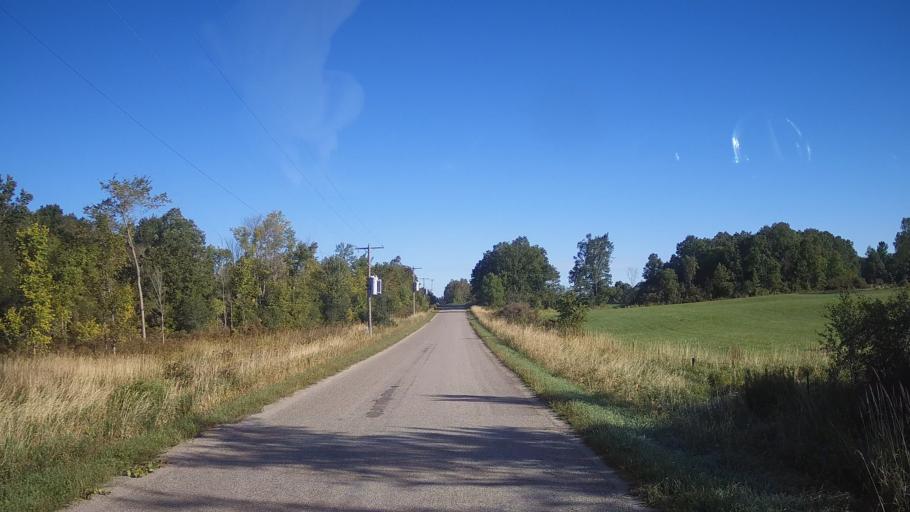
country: US
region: New York
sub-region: Jefferson County
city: Alexandria Bay
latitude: 44.4188
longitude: -75.9778
